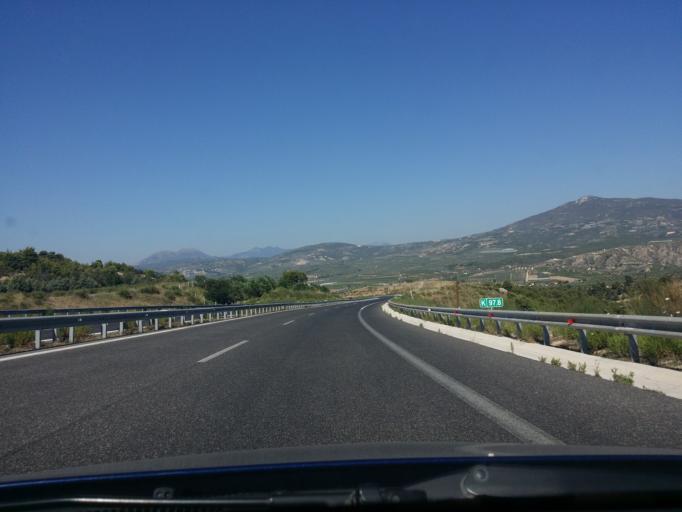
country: GR
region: Peloponnese
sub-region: Nomos Korinthias
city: Ayios Vasilios
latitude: 37.8475
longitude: 22.8235
